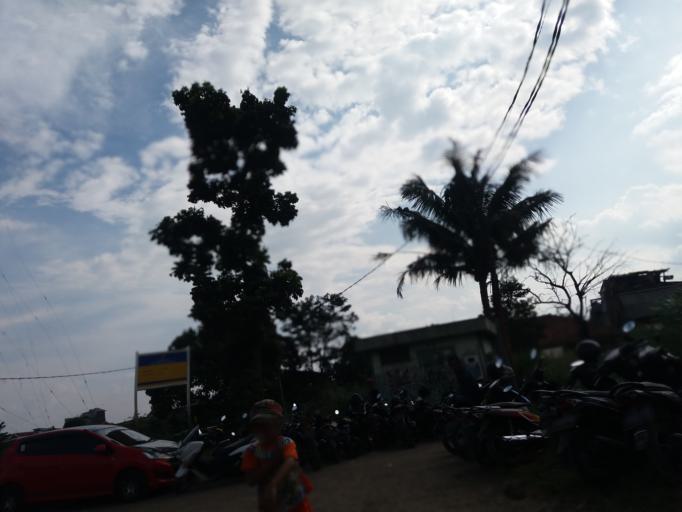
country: ID
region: West Java
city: Bandung
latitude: -6.9227
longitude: 107.6486
